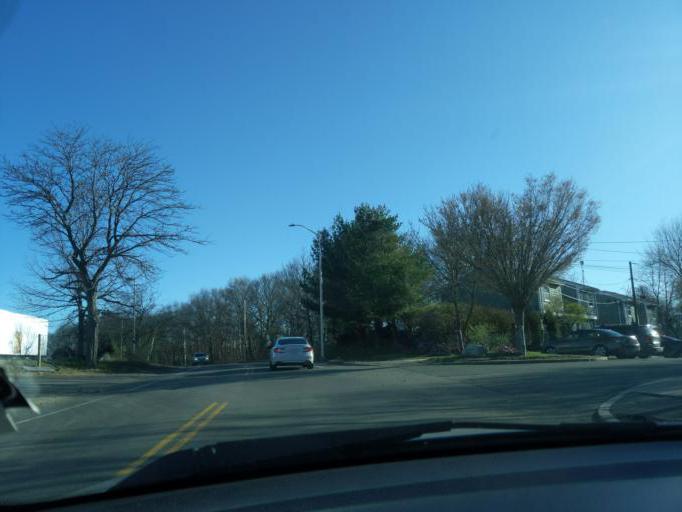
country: US
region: Massachusetts
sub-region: Essex County
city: Beverly
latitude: 42.5684
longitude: -70.8787
